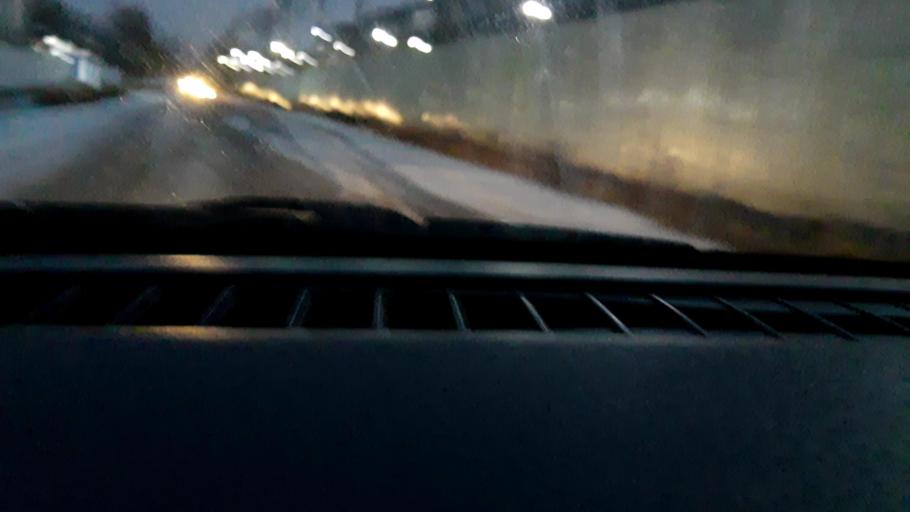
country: RU
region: Nizjnij Novgorod
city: Nizhniy Novgorod
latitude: 56.3068
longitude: 43.8849
